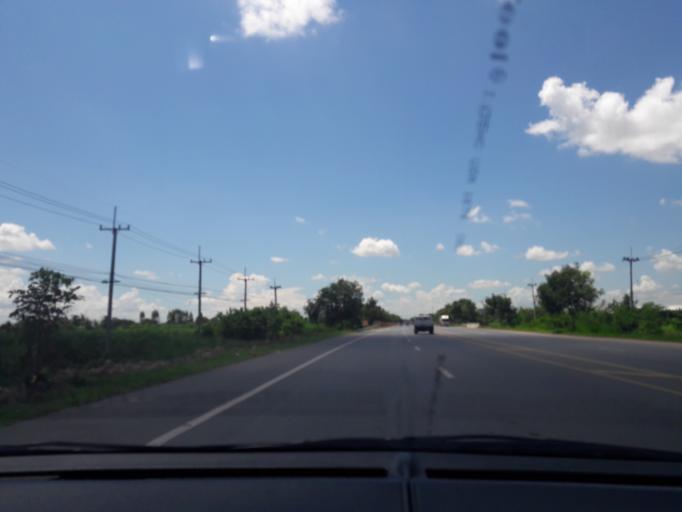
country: TH
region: Kanchanaburi
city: Tha Maka
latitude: 14.0316
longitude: 99.8313
